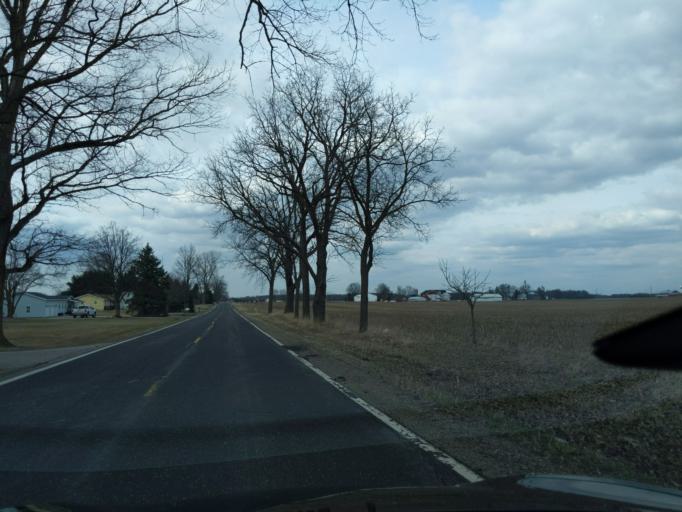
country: US
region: Michigan
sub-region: Ingham County
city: Mason
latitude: 42.5765
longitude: -84.4834
